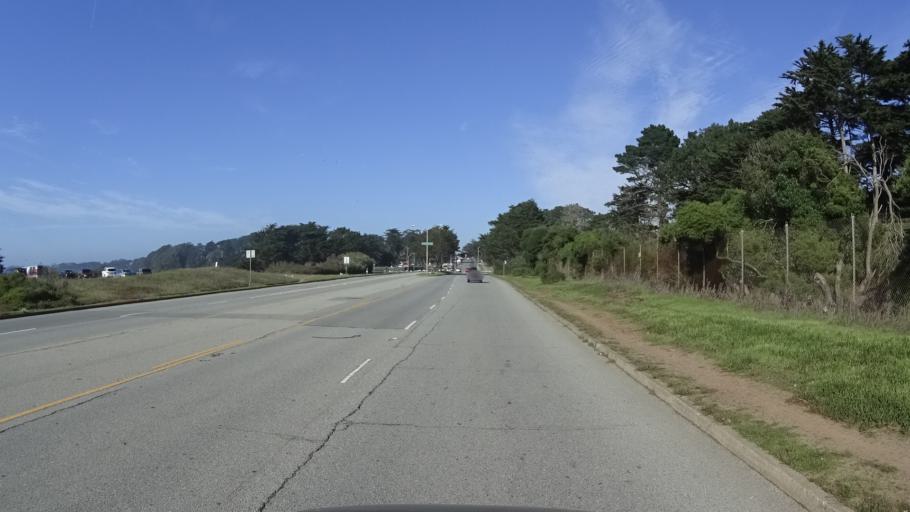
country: US
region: California
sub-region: San Mateo County
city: Daly City
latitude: 37.7128
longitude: -122.4852
